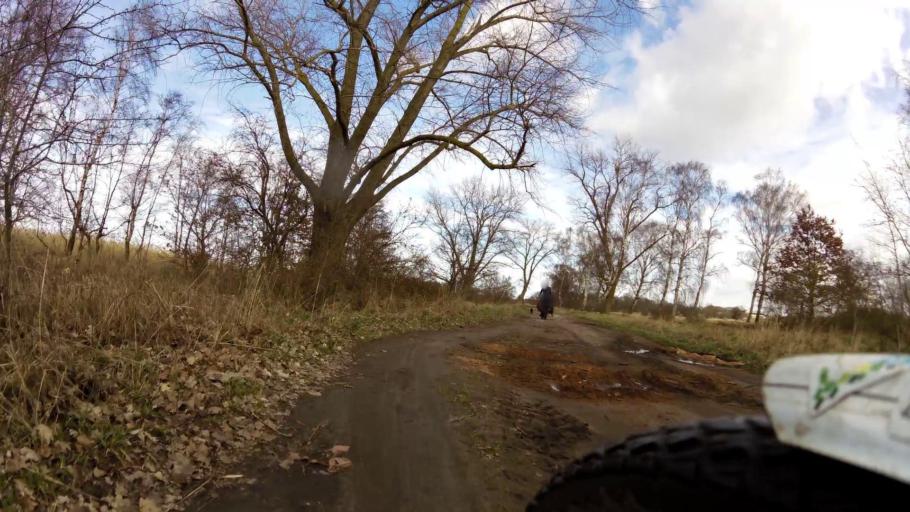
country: PL
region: West Pomeranian Voivodeship
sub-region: Powiat kamienski
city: Dziwnow
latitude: 54.0080
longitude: 14.8020
